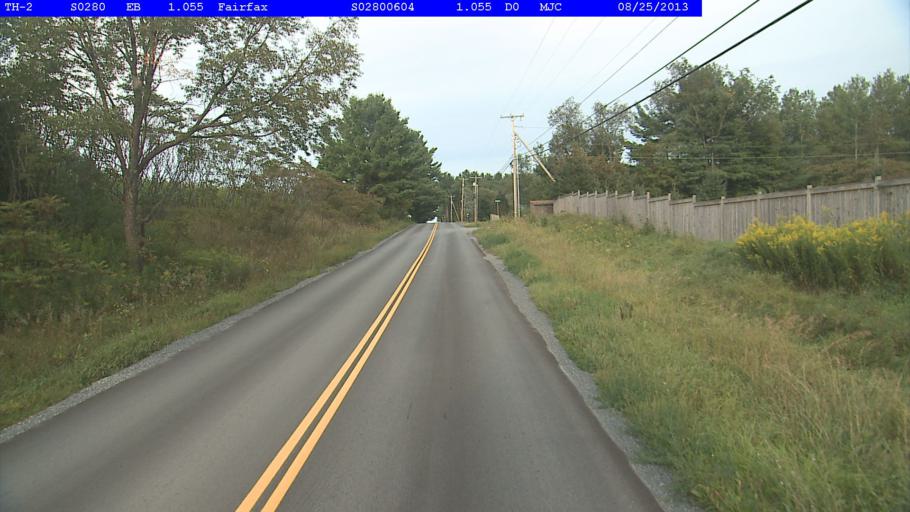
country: US
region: Vermont
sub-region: Chittenden County
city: Milton
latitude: 44.6701
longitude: -72.9909
